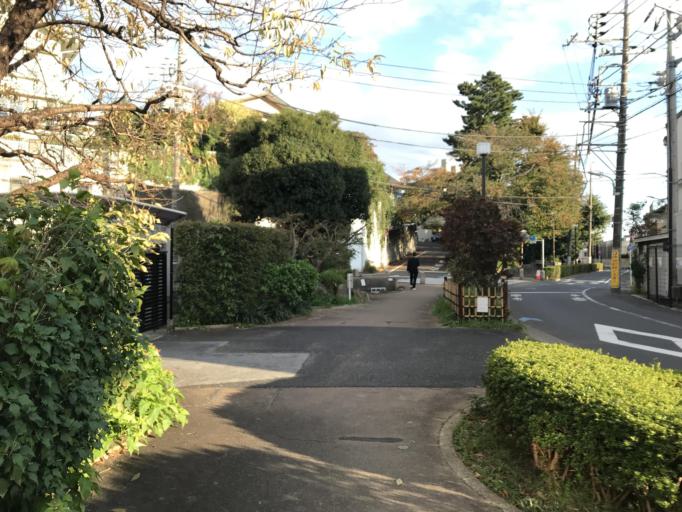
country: JP
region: Kanagawa
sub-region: Kawasaki-shi
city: Kawasaki
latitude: 35.5807
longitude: 139.6772
